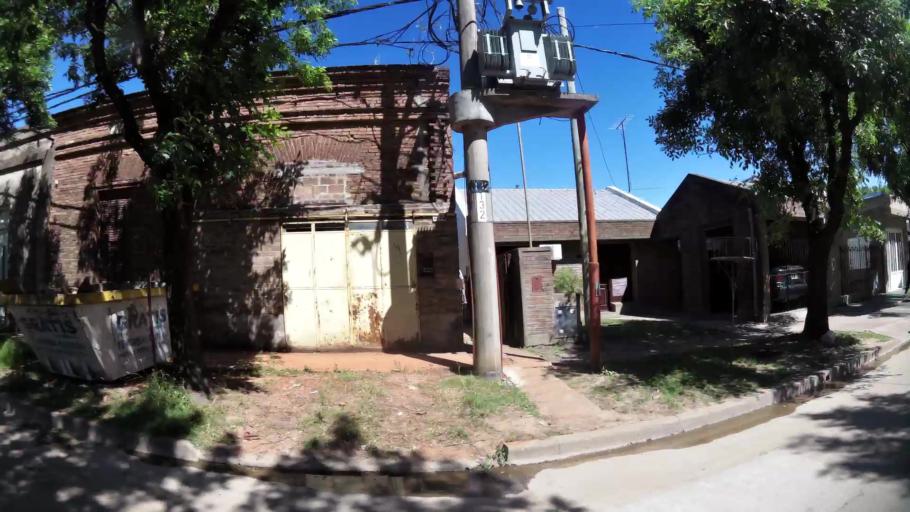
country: AR
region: Santa Fe
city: Esperanza
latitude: -31.4389
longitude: -60.9252
